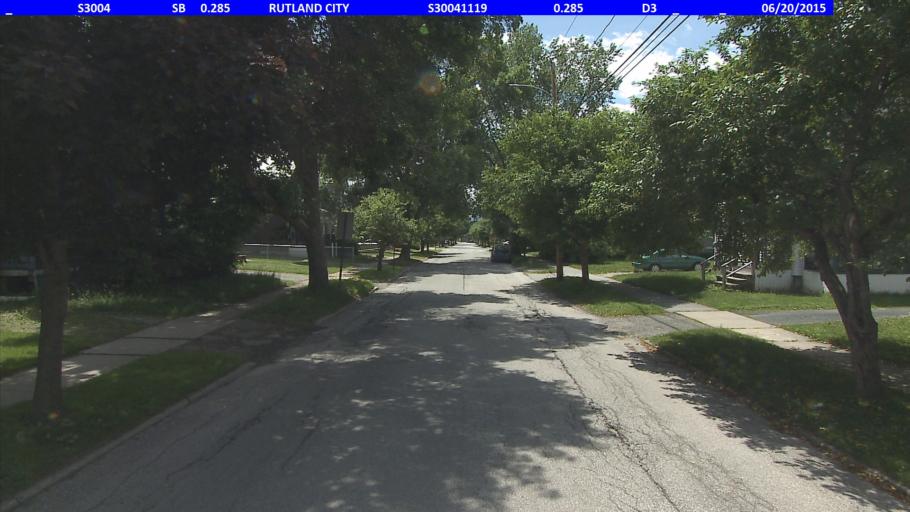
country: US
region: Vermont
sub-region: Rutland County
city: Rutland
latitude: 43.6120
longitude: -72.9789
